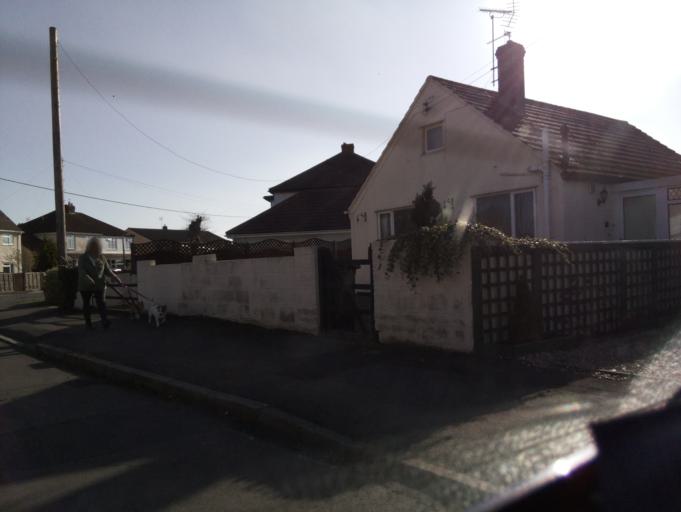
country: GB
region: England
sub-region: South Gloucestershire
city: Yate
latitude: 51.5394
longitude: -2.4255
